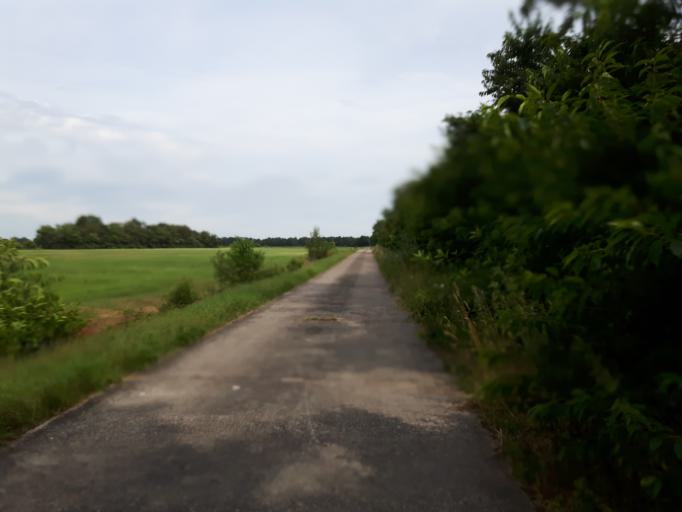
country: DE
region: Lower Saxony
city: Rastede
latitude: 53.2918
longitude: 8.2923
